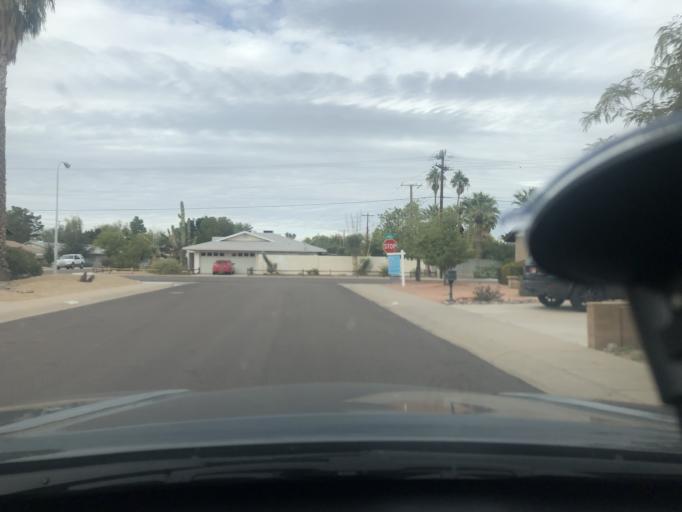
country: US
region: Arizona
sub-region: Maricopa County
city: Scottsdale
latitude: 33.4836
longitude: -111.9039
